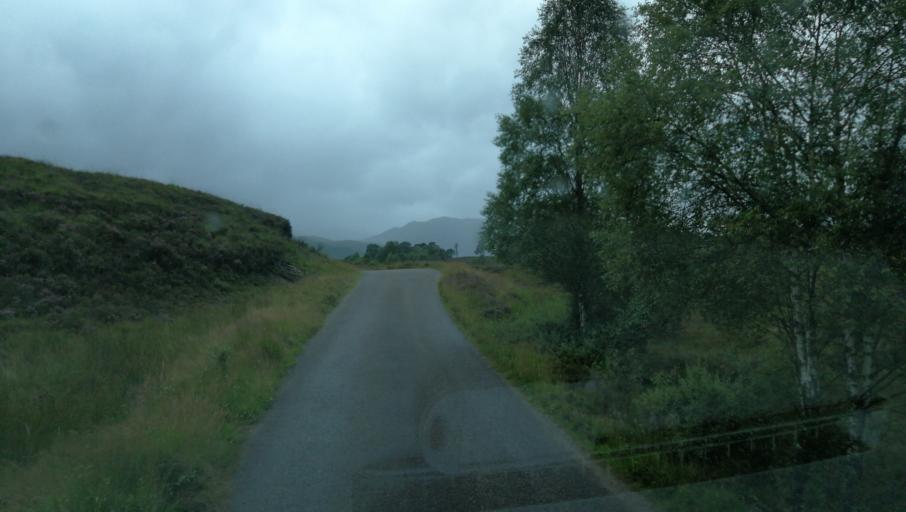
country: GB
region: Scotland
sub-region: Highland
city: Spean Bridge
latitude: 57.2722
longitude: -4.9629
